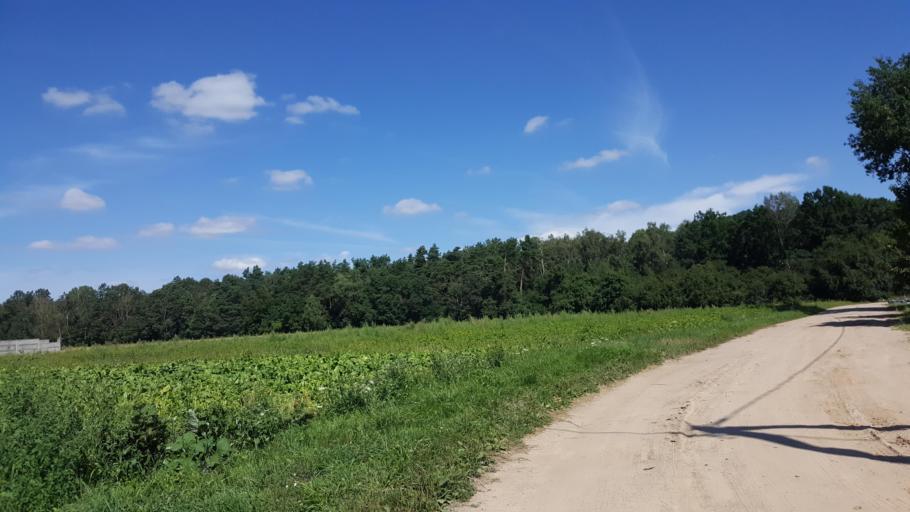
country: BY
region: Brest
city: Charnawchytsy
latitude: 52.3676
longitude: 23.6219
